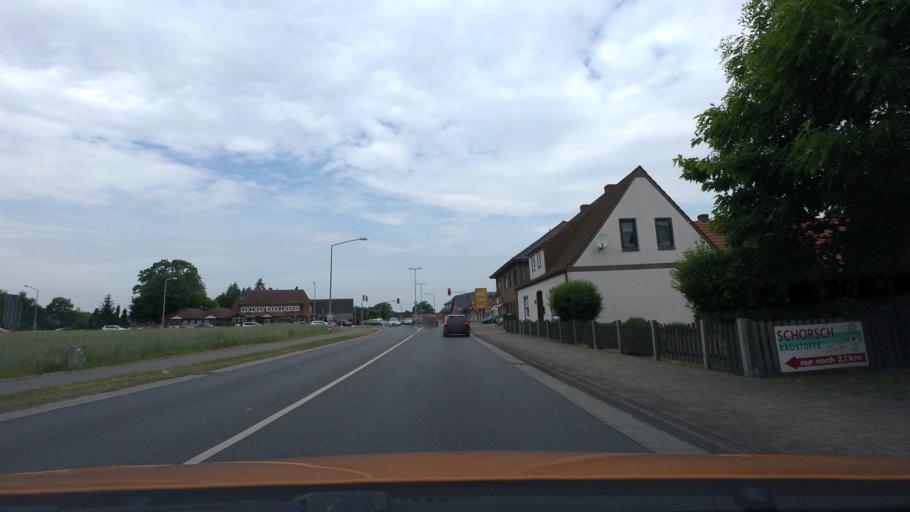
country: DE
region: Lower Saxony
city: Stuhr
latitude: 52.9949
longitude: 8.7672
